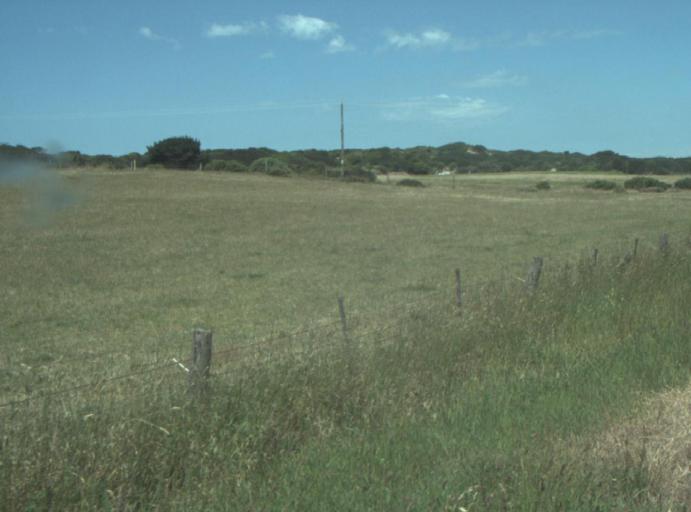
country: AU
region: Victoria
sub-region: Greater Geelong
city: Leopold
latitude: -38.2761
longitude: 144.4352
